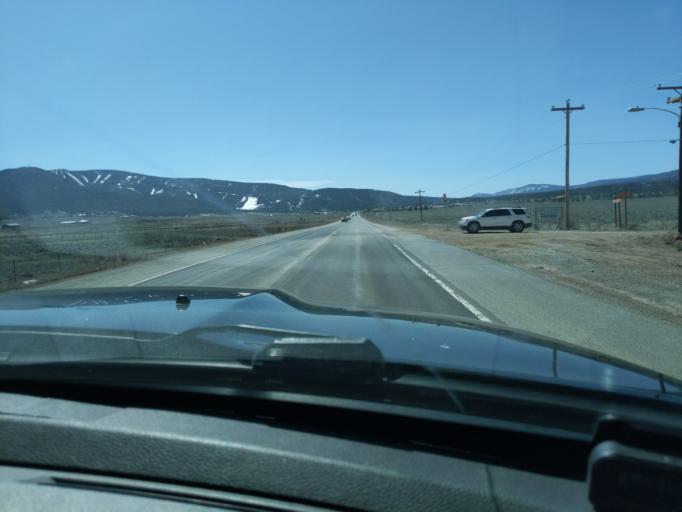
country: US
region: New Mexico
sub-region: Colfax County
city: Angel Fire
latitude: 36.4219
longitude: -105.2976
